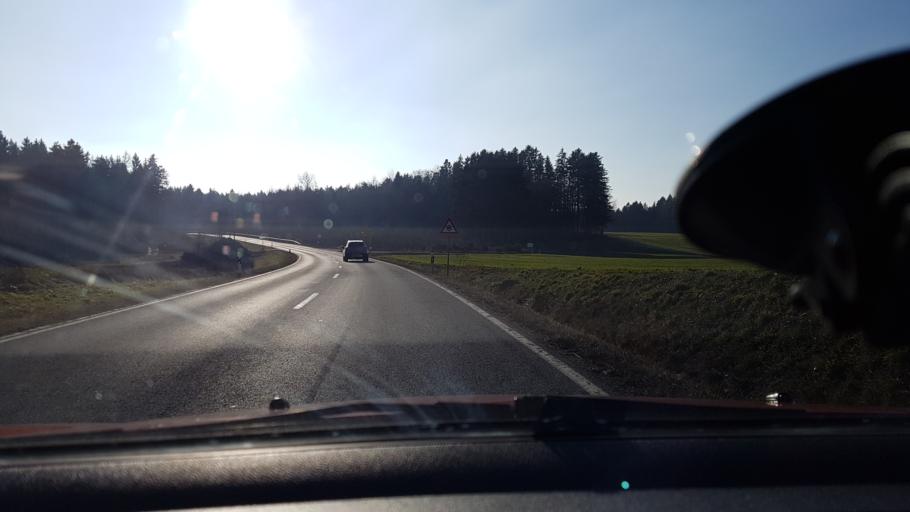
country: DE
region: Bavaria
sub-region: Lower Bavaria
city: Wittibreut
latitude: 48.3569
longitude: 12.9584
